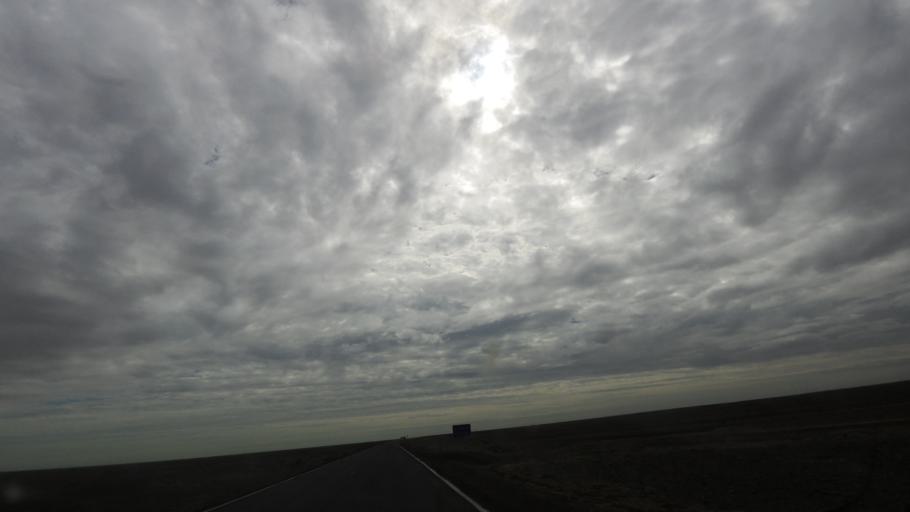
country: IS
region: East
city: Hoefn
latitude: 63.9828
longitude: -16.9619
